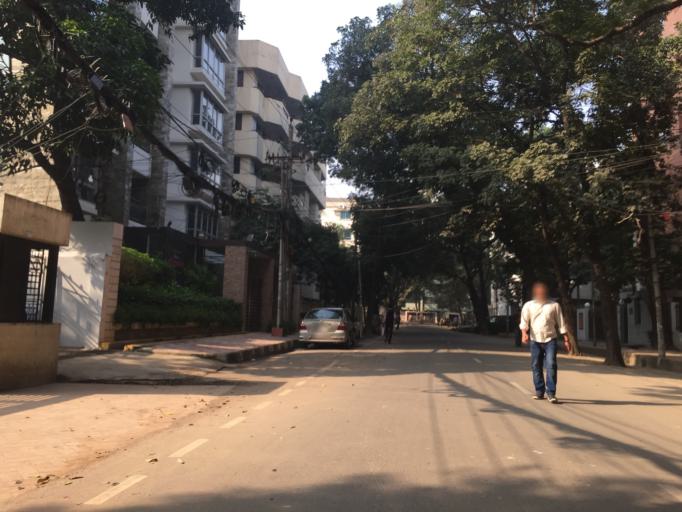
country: BD
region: Dhaka
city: Paltan
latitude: 23.7948
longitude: 90.4175
